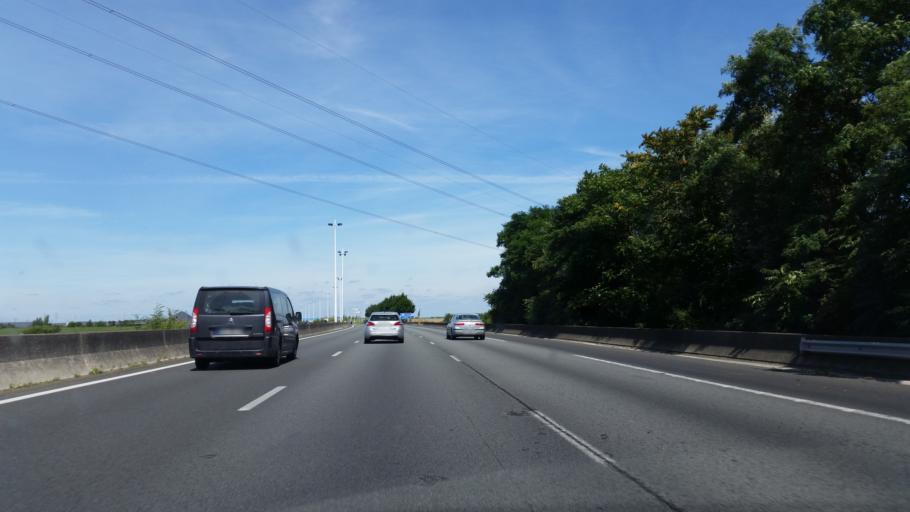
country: FR
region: Nord-Pas-de-Calais
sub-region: Departement du Pas-de-Calais
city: Henin-Beaumont
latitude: 50.3861
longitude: 2.9810
